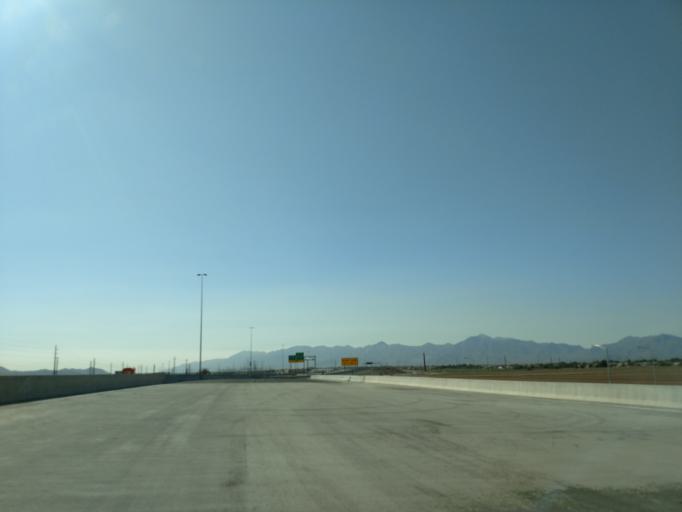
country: US
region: Arizona
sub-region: Maricopa County
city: Laveen
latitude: 33.4302
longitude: -112.1874
